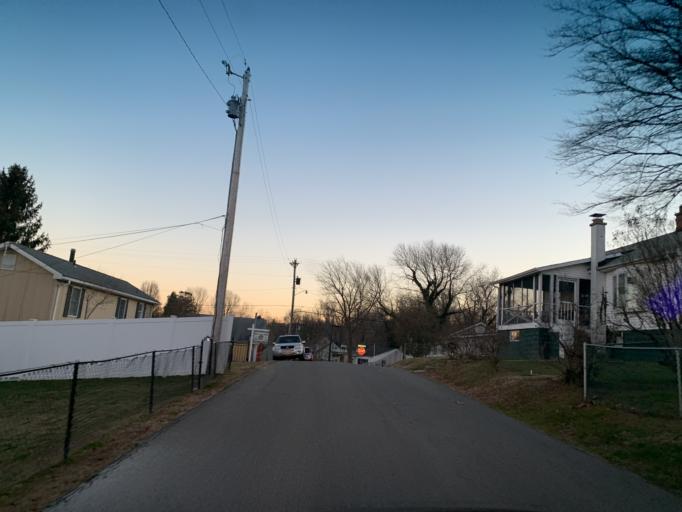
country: US
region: Maryland
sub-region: Calvert County
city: Prince Frederick
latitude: 38.5604
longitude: -76.5176
